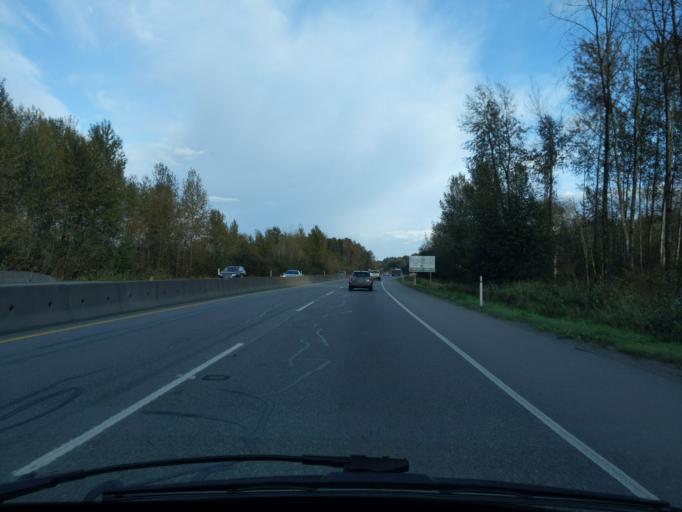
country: CA
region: British Columbia
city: Port Moody
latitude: 49.2136
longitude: -122.8083
